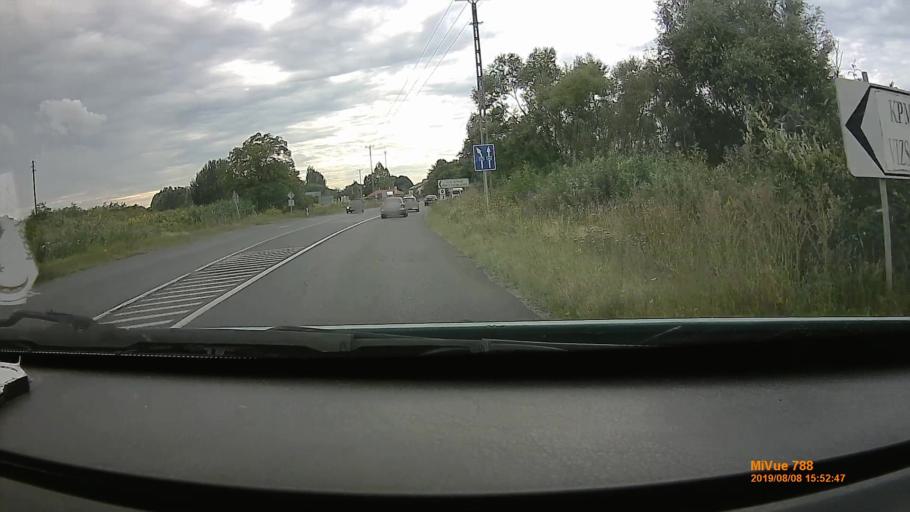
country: HU
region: Szabolcs-Szatmar-Bereg
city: Mateszalka
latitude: 47.9401
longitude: 22.3299
